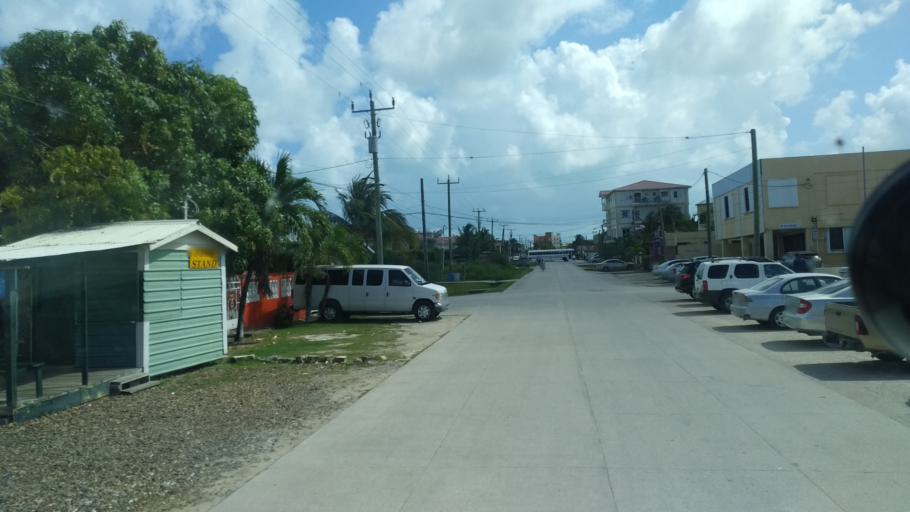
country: BZ
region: Belize
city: Belize City
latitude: 17.5129
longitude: -88.2032
